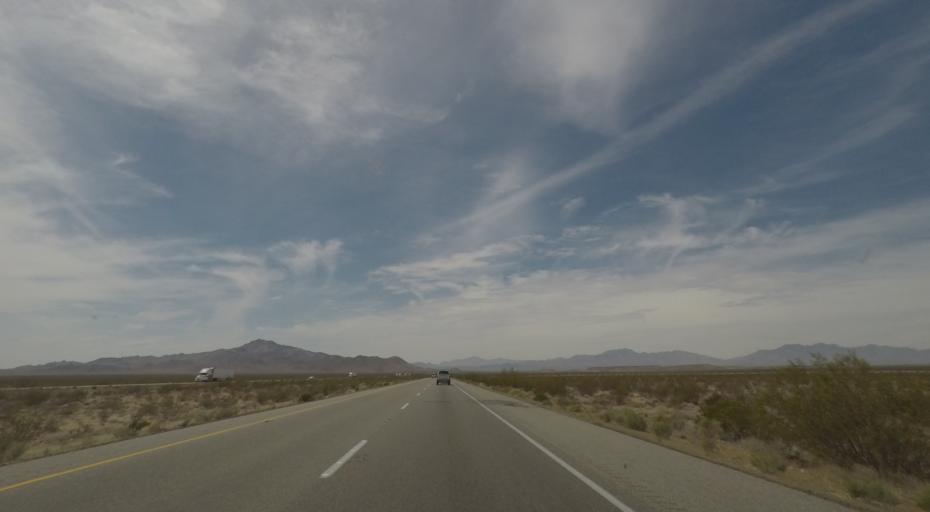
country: US
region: California
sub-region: San Bernardino County
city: Needles
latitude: 34.8072
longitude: -115.2490
